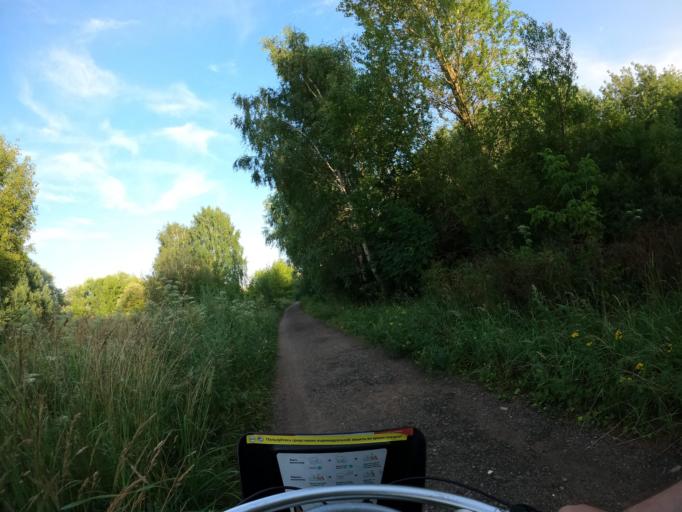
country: RU
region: Moscow
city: Strogino
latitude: 55.8242
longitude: 37.4048
